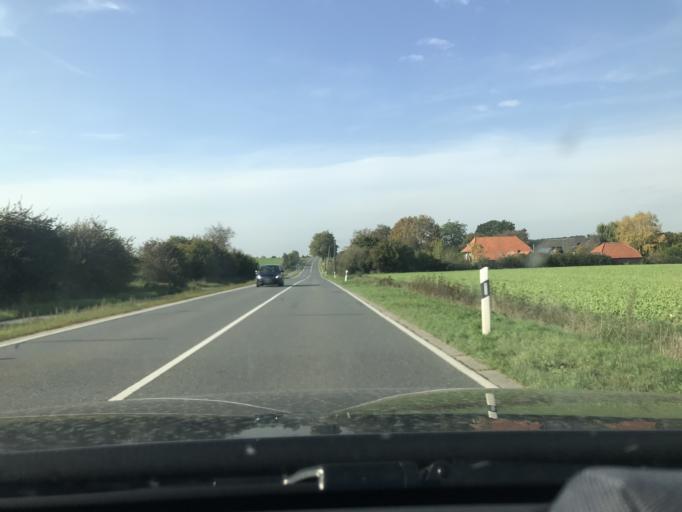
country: DE
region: North Rhine-Westphalia
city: Kalkar
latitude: 51.7347
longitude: 6.2601
